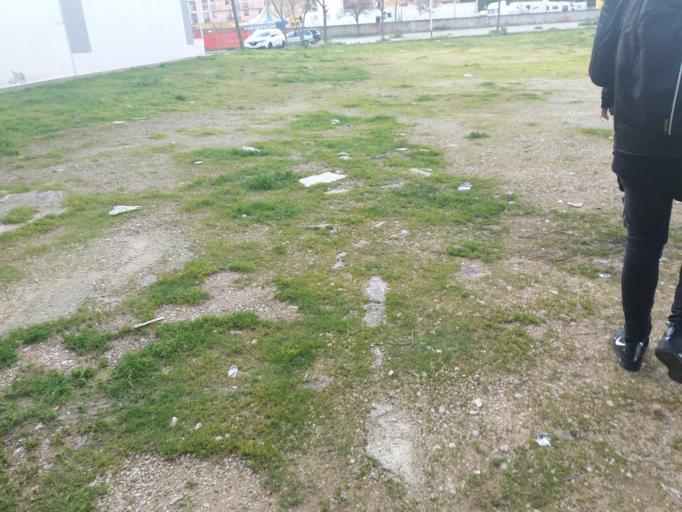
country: IT
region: Apulia
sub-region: Provincia di Barletta - Andria - Trani
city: Andria
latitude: 41.2384
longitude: 16.2918
